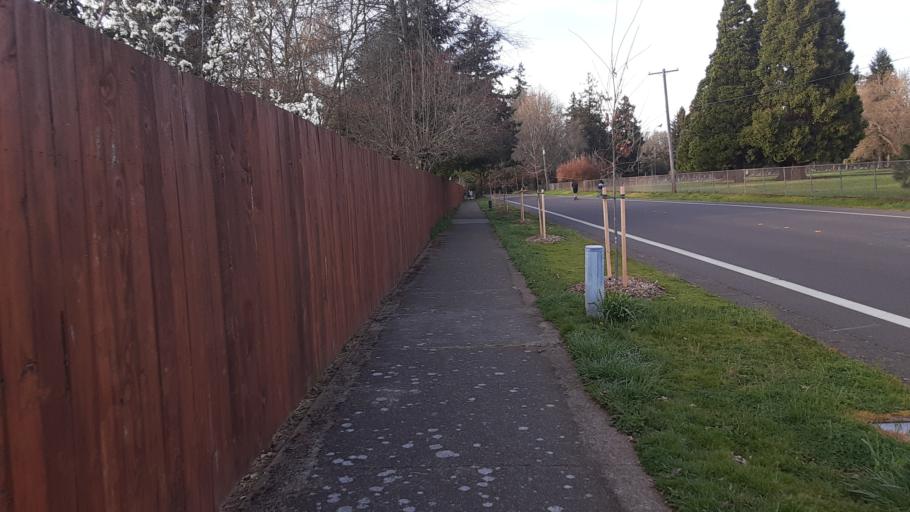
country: US
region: Oregon
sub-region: Benton County
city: Corvallis
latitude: 44.5465
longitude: -123.2558
